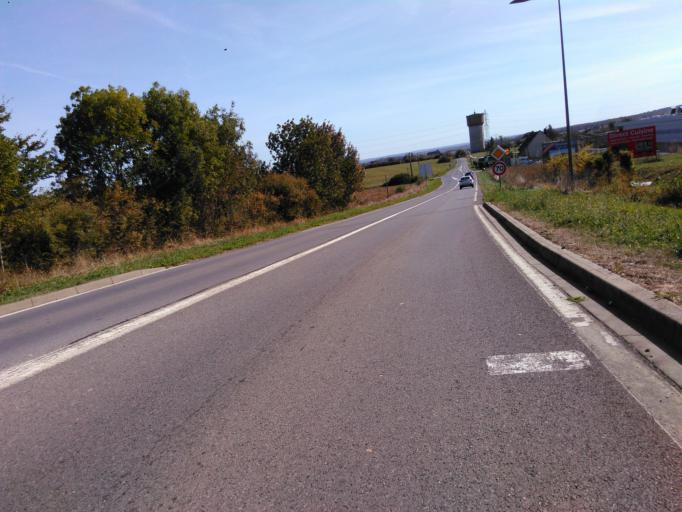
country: FR
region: Lorraine
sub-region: Departement de la Moselle
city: Hettange-Grande
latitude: 49.4176
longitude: 6.1383
